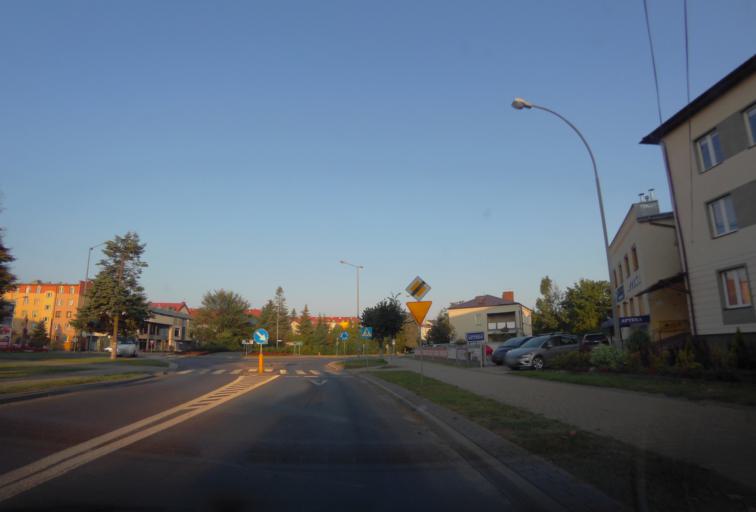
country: PL
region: Lublin Voivodeship
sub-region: Powiat janowski
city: Janow Lubelski
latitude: 50.7010
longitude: 22.4218
